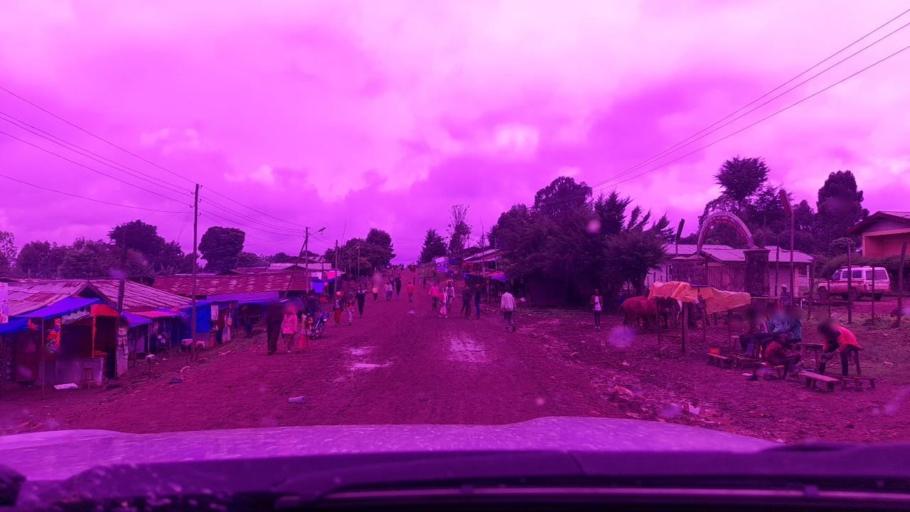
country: ET
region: Southern Nations, Nationalities, and People's Region
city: Tippi
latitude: 7.5936
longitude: 35.7533
